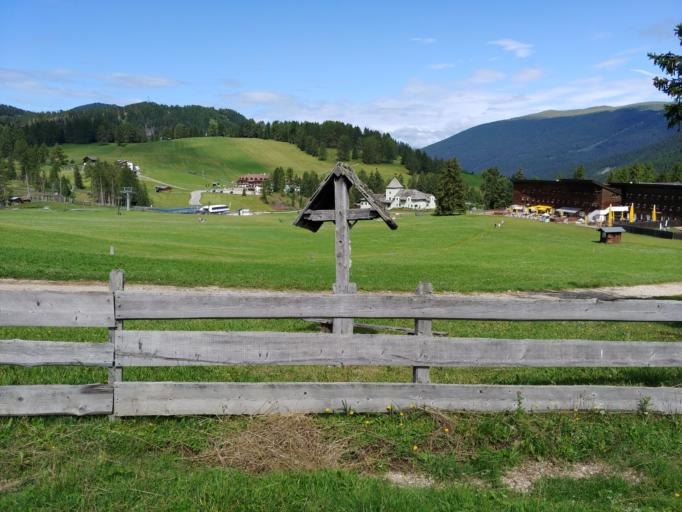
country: IT
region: Trentino-Alto Adige
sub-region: Bolzano
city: Santa Cristina Valgardena
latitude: 46.5495
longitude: 11.7199
